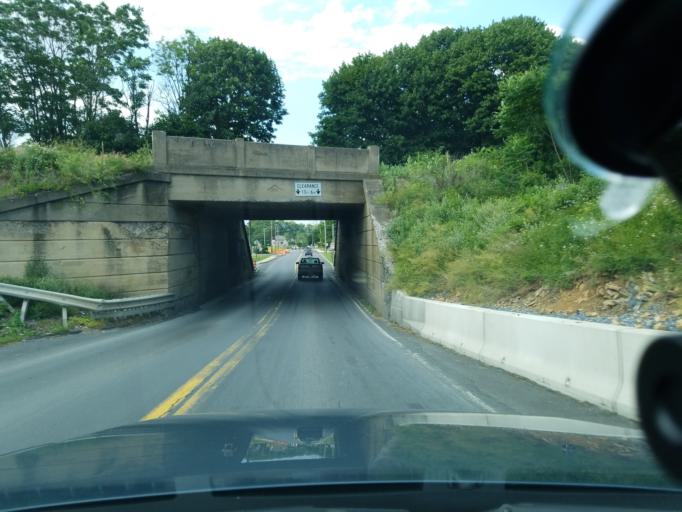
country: US
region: Pennsylvania
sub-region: Lebanon County
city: Myerstown
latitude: 40.3646
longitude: -76.3072
